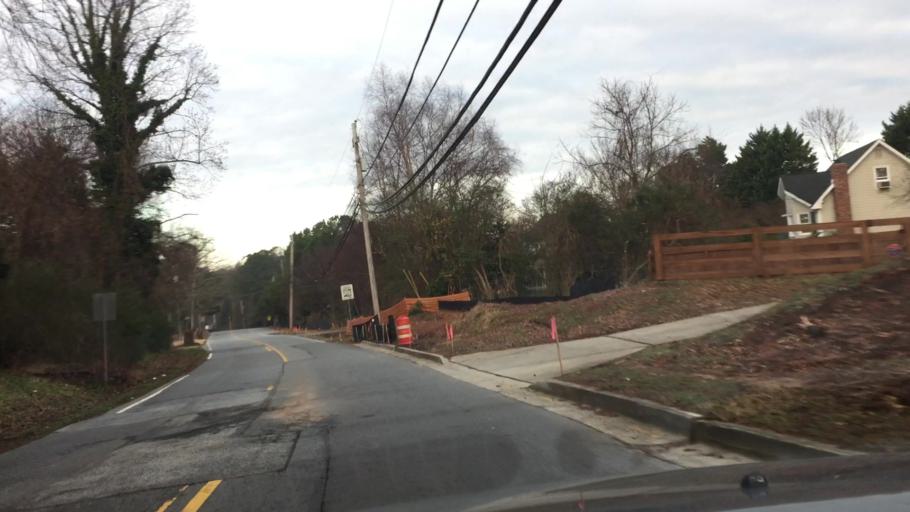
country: US
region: Georgia
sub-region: DeKalb County
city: Doraville
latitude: 33.9547
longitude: -84.2732
